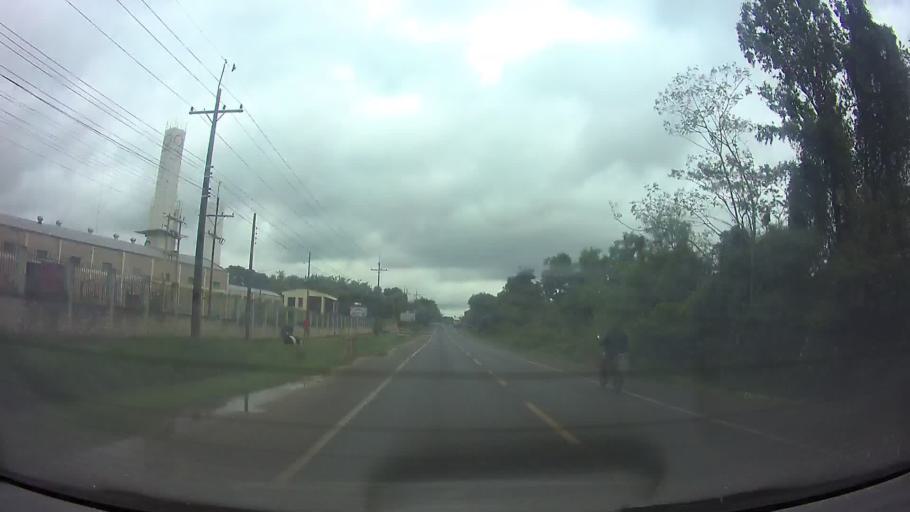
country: PY
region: Central
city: Guarambare
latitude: -25.4995
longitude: -57.4847
